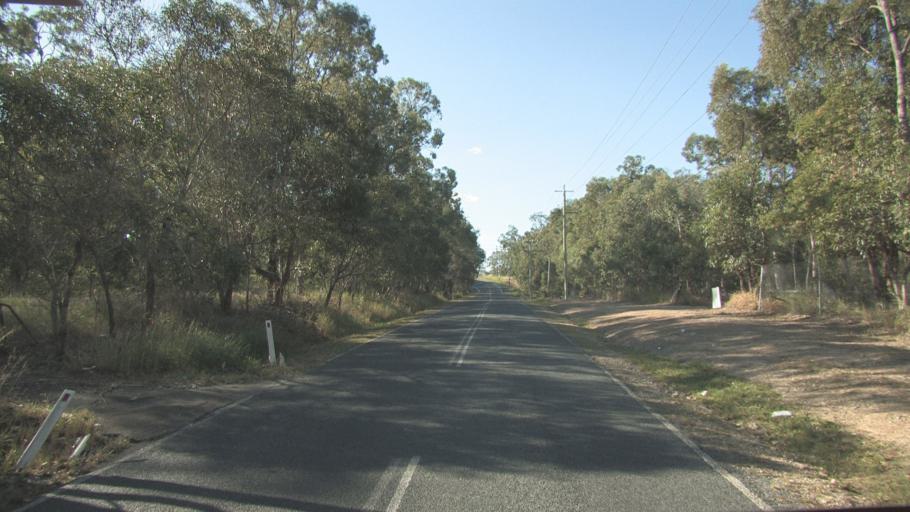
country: AU
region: Queensland
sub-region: Logan
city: Windaroo
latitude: -27.7283
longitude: 153.1719
